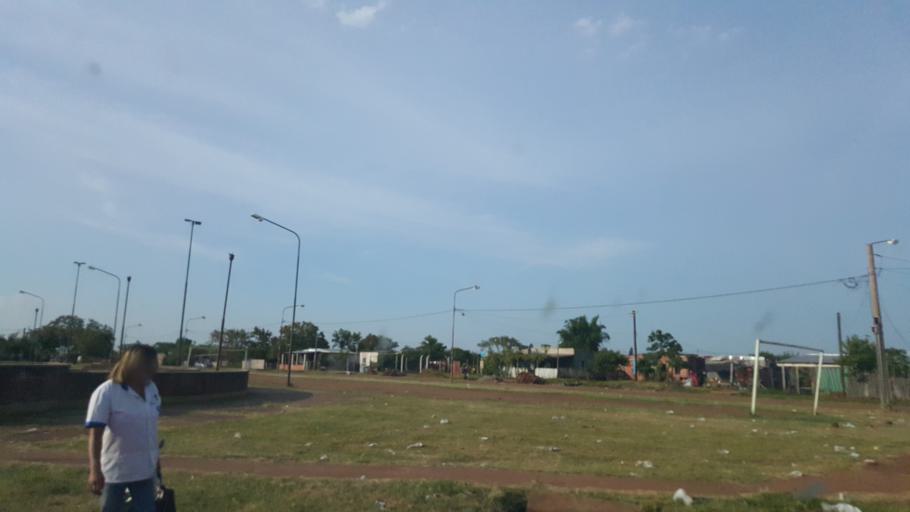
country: AR
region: Misiones
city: Garupa
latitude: -27.4346
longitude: -55.8671
